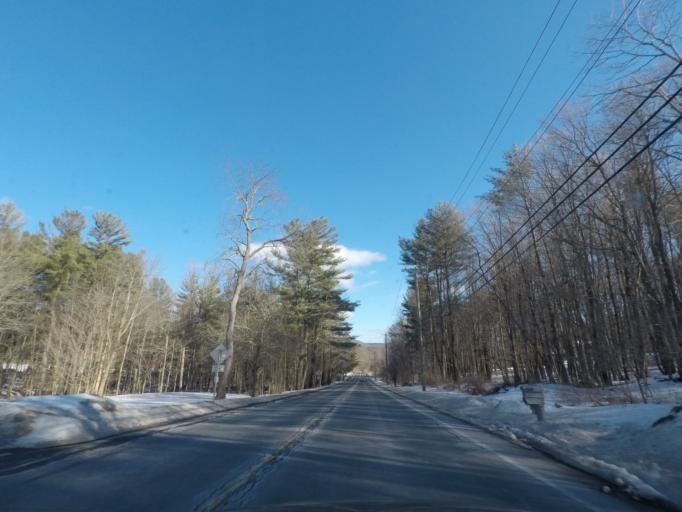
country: US
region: New York
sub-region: Columbia County
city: Chatham
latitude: 42.3197
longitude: -73.4908
